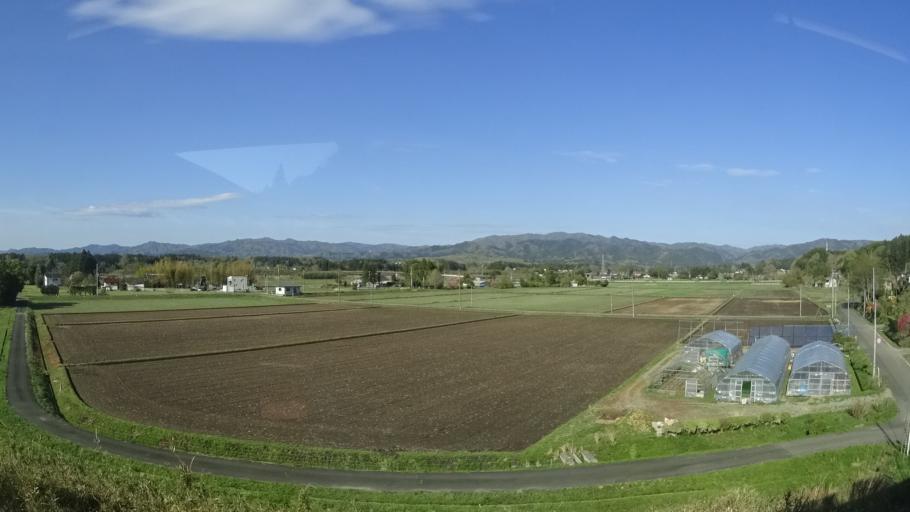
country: JP
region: Fukushima
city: Namie
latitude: 37.5047
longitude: 140.9778
